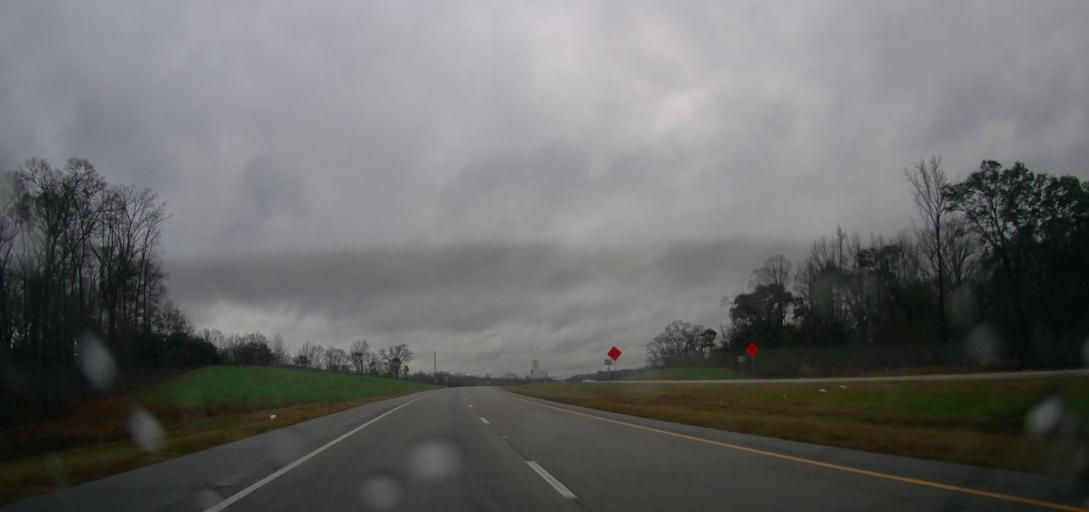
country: US
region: Alabama
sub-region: Bibb County
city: Centreville
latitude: 32.9394
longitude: -87.0687
